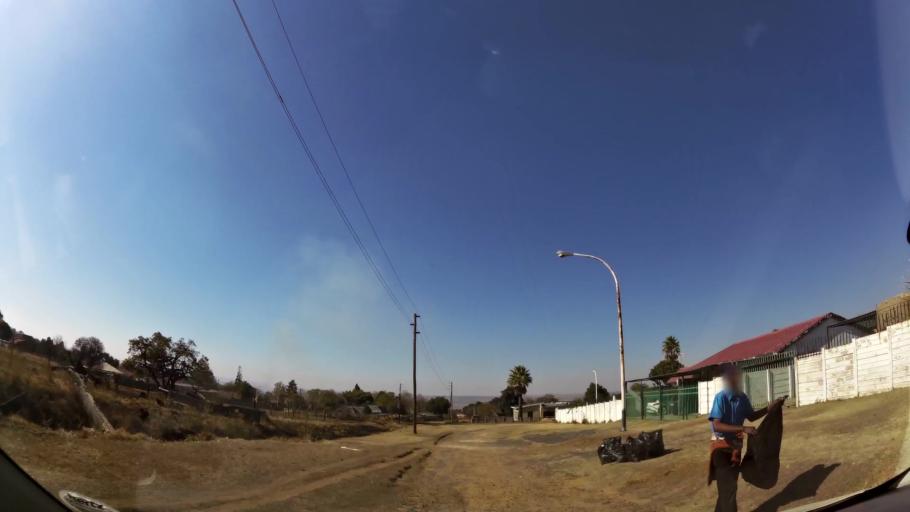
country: ZA
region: Mpumalanga
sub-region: Nkangala District Municipality
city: Witbank
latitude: -25.8304
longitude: 29.2406
